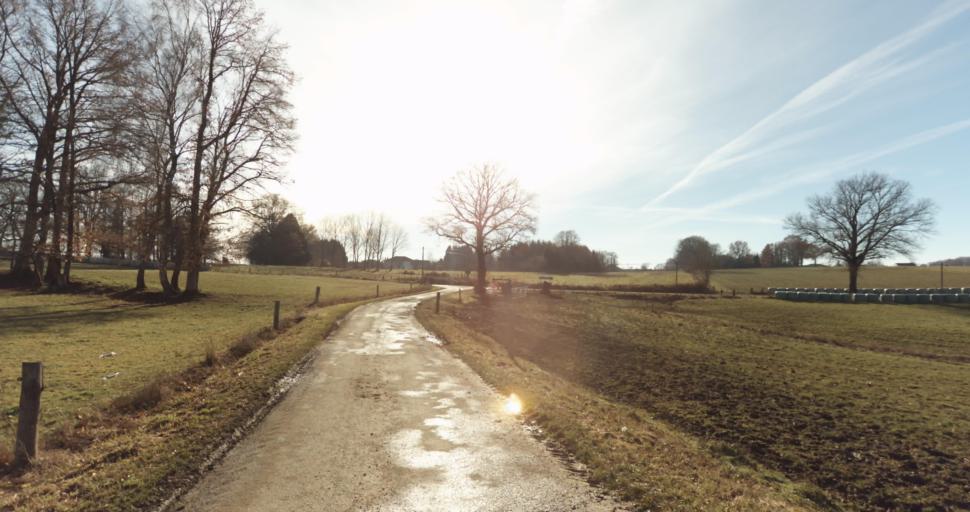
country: FR
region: Limousin
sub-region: Departement de la Haute-Vienne
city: Sereilhac
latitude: 45.7796
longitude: 1.0916
